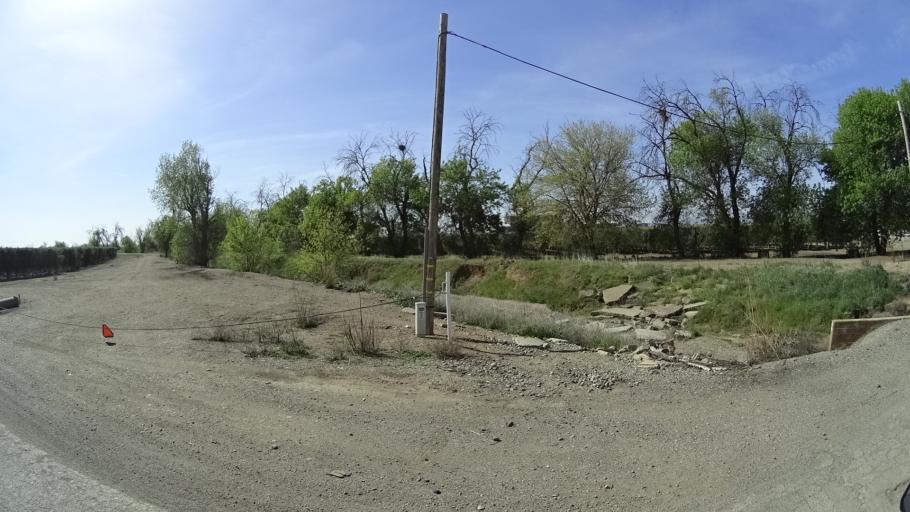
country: US
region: California
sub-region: Glenn County
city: Willows
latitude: 39.6116
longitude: -122.2603
